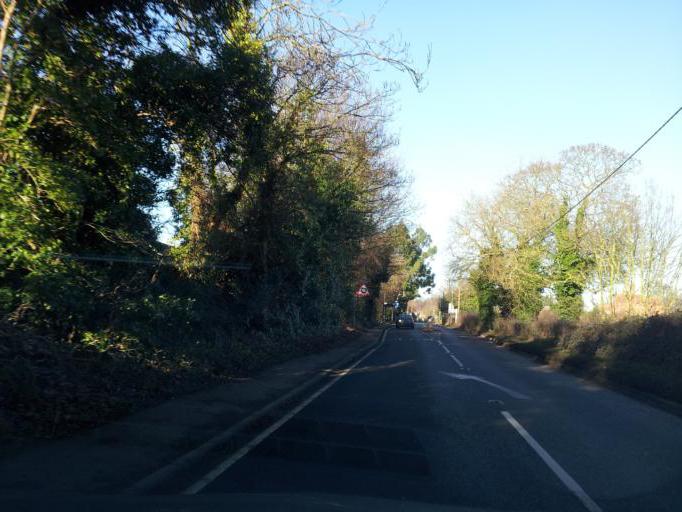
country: GB
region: England
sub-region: Essex
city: Great Horkesley
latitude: 51.9276
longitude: 0.8799
